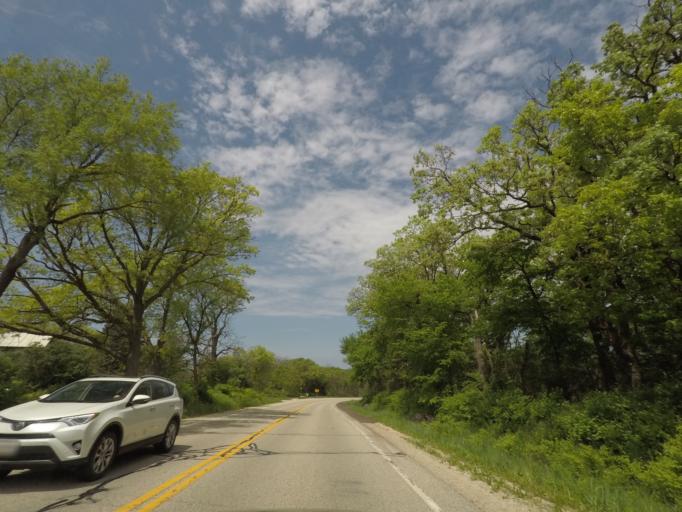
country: US
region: Wisconsin
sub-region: Rock County
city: Orfordville
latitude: 42.6487
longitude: -89.2865
